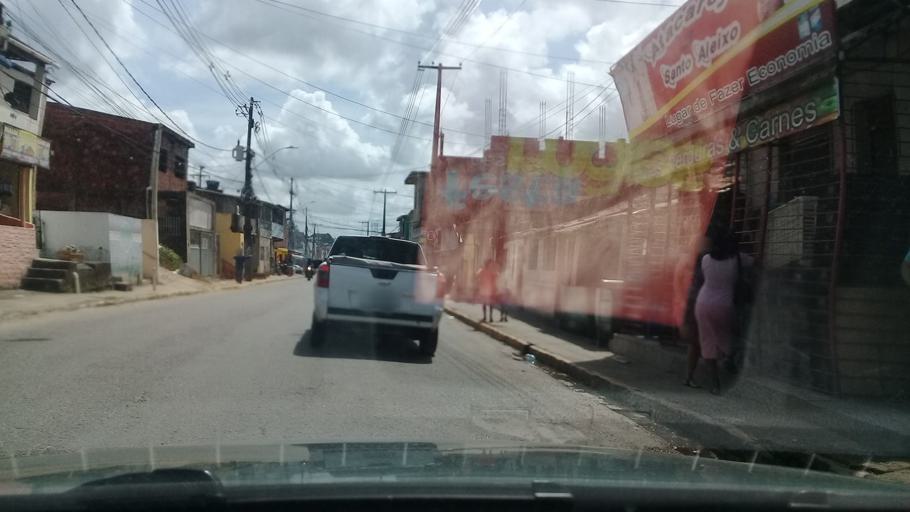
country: BR
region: Pernambuco
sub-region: Jaboatao Dos Guararapes
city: Jaboatao dos Guararapes
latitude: -8.1008
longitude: -35.0199
